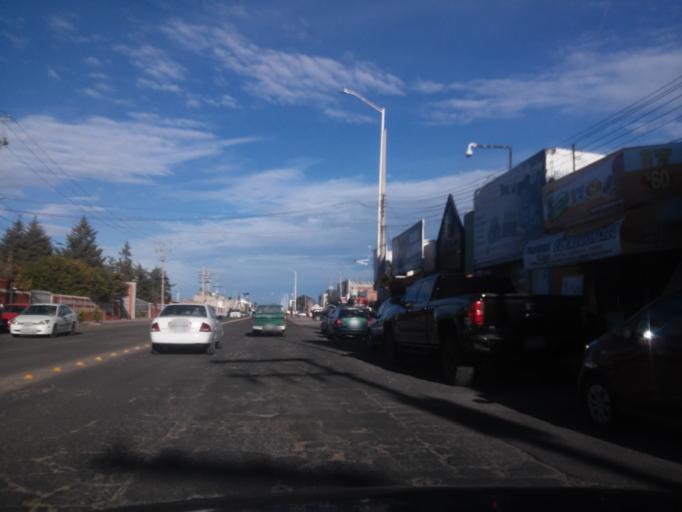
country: MX
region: Durango
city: Victoria de Durango
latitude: 24.0038
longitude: -104.6498
